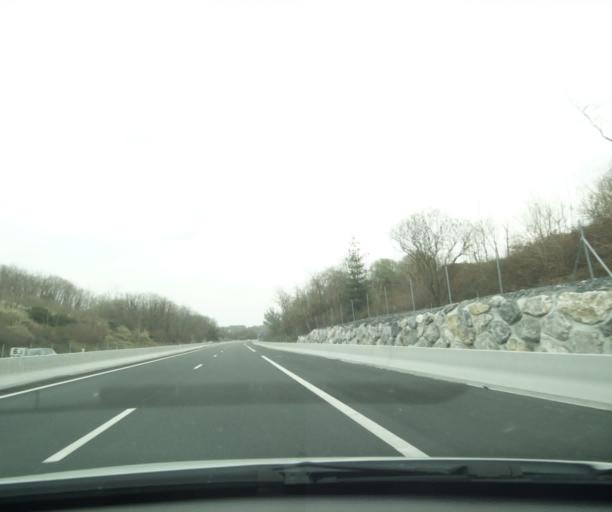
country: FR
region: Aquitaine
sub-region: Departement des Pyrenees-Atlantiques
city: Lahonce
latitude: 43.4530
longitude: -1.3912
